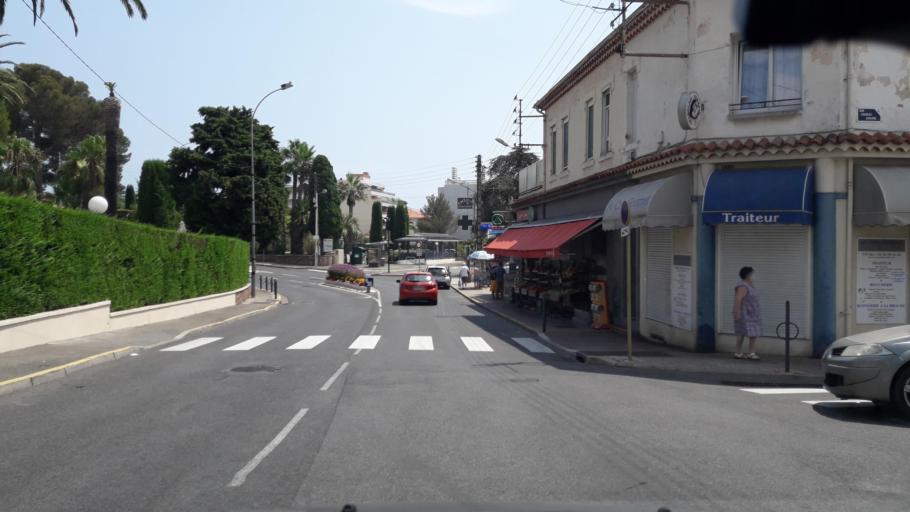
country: FR
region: Provence-Alpes-Cote d'Azur
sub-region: Departement du Var
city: Saint-Raphael
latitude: 43.4173
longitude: 6.8078
